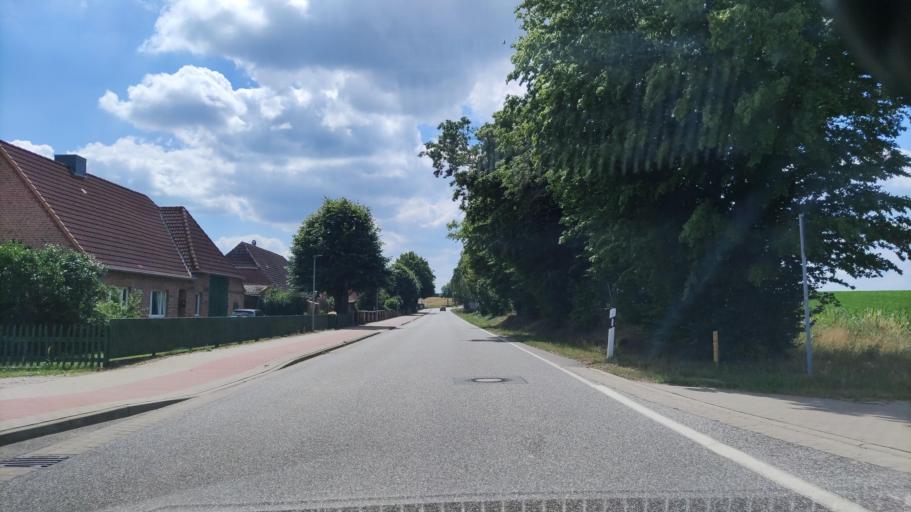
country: DE
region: Mecklenburg-Vorpommern
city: Hagenow
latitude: 53.4057
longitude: 11.1699
